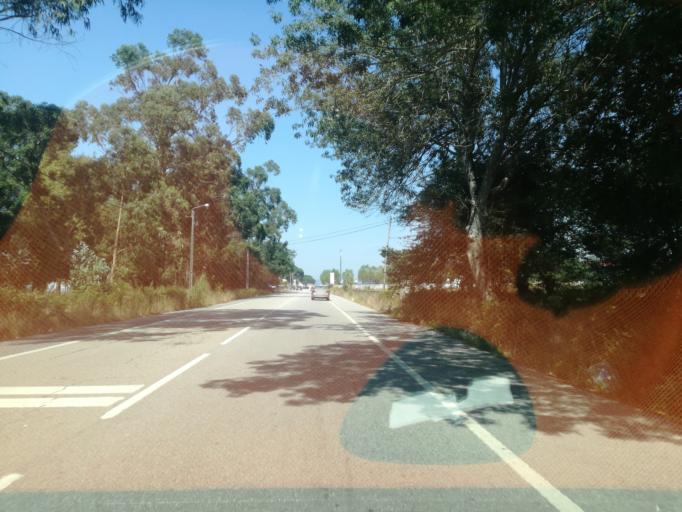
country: PT
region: Braga
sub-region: Esposende
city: Apulia
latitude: 41.4573
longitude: -8.7503
